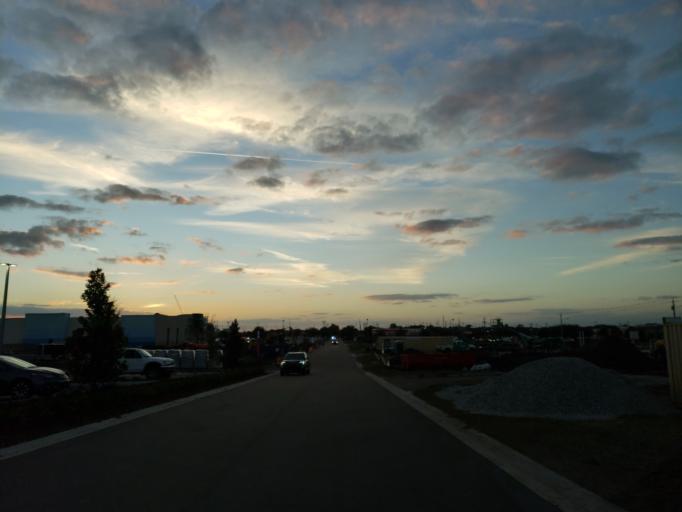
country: US
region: Florida
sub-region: Hillsborough County
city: Balm
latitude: 27.7913
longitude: -82.3290
